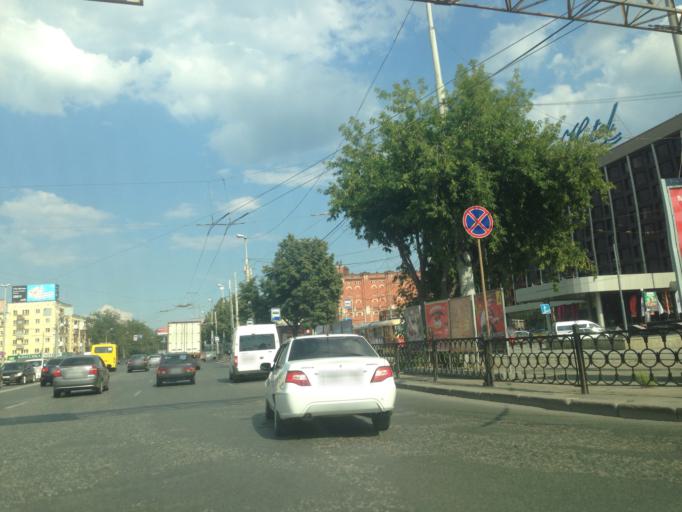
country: RU
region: Sverdlovsk
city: Yekaterinburg
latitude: 56.8564
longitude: 60.6041
